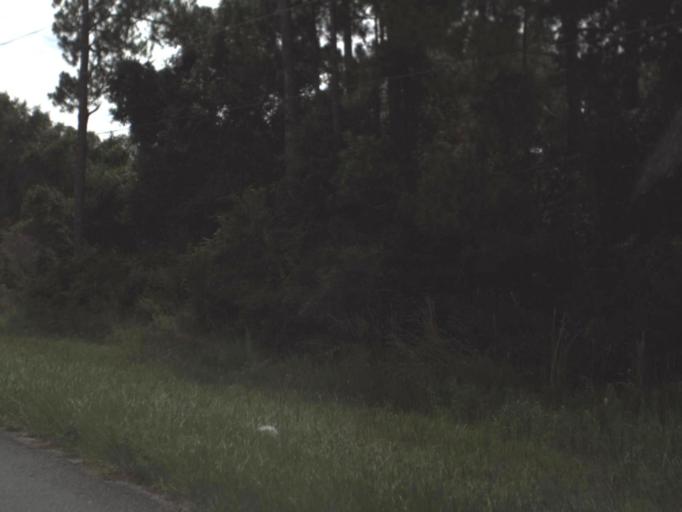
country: US
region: Florida
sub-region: Citrus County
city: Hernando
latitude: 28.9716
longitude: -82.3670
